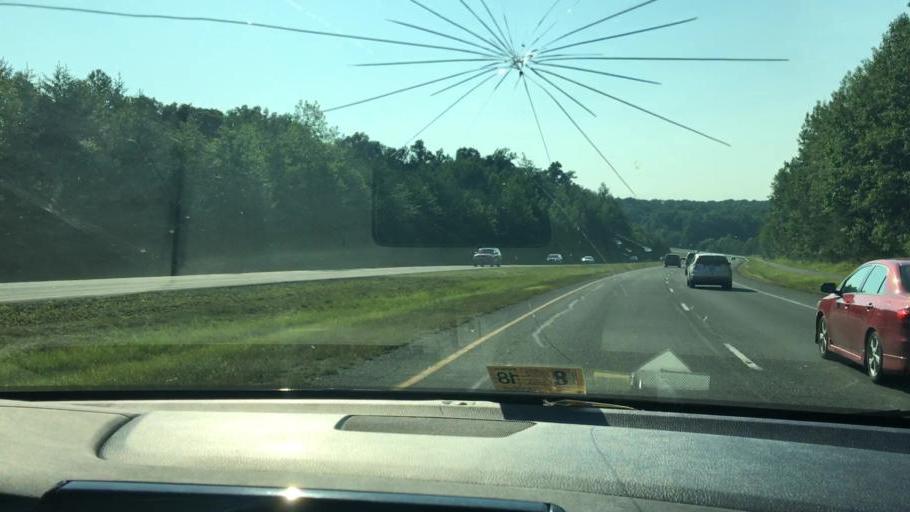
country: US
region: Virginia
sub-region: Prince William County
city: Lake Ridge
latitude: 38.6837
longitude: -77.3717
